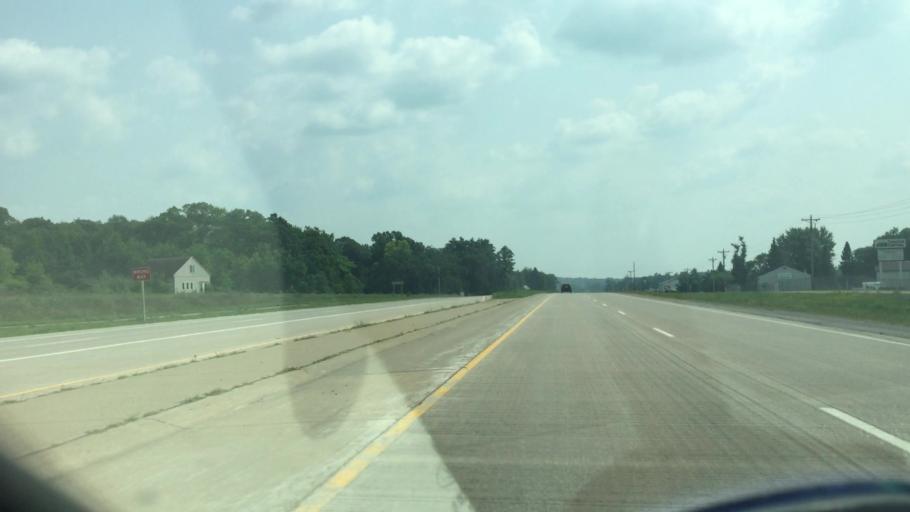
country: US
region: Wisconsin
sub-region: Eau Claire County
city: Altoona
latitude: 44.7517
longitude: -91.4539
